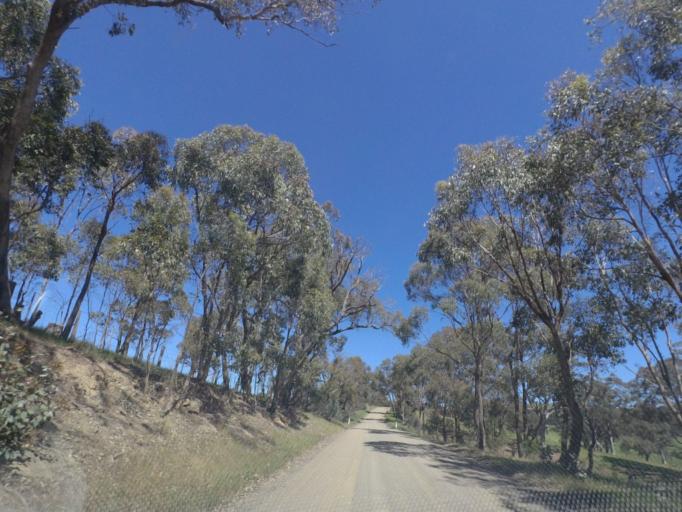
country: AU
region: Victoria
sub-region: Whittlesea
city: Whittlesea
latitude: -37.2758
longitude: 145.0191
